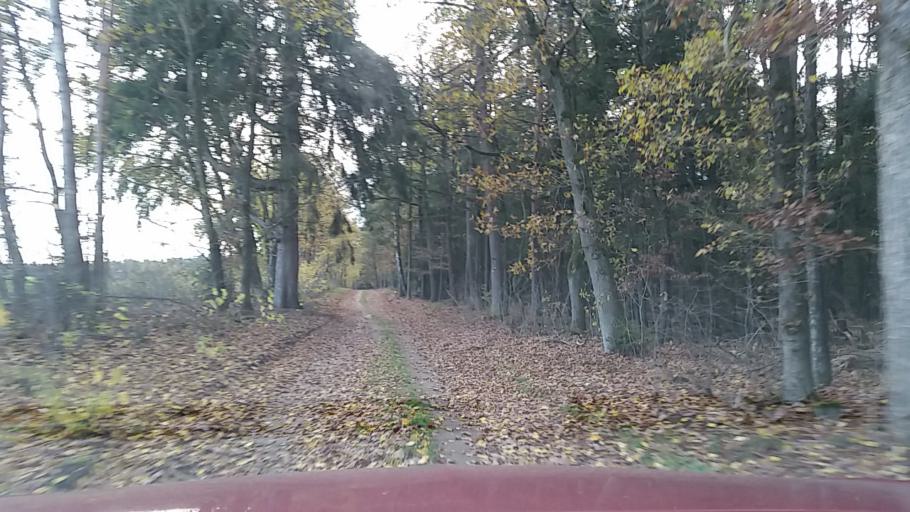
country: DE
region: Lower Saxony
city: Sprakensehl
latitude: 52.8083
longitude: 10.5198
